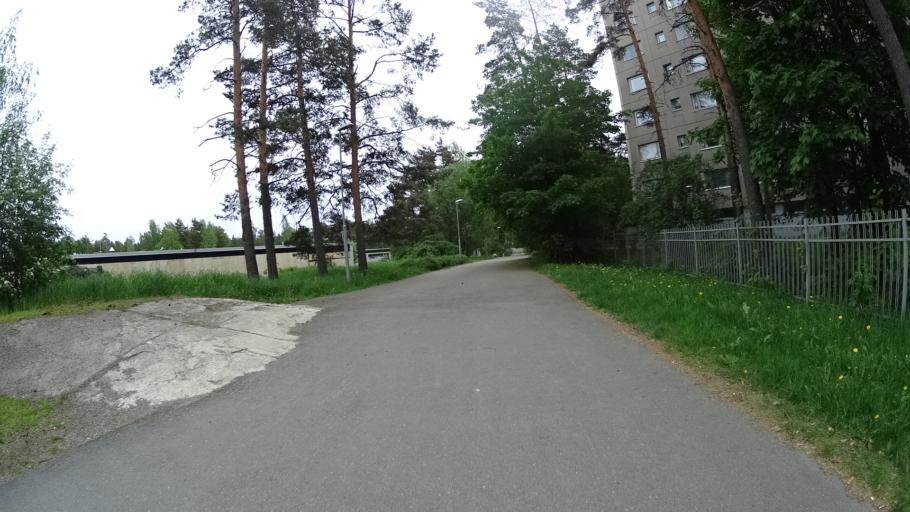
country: FI
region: Uusimaa
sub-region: Helsinki
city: Vantaa
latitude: 60.2418
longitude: 25.0761
